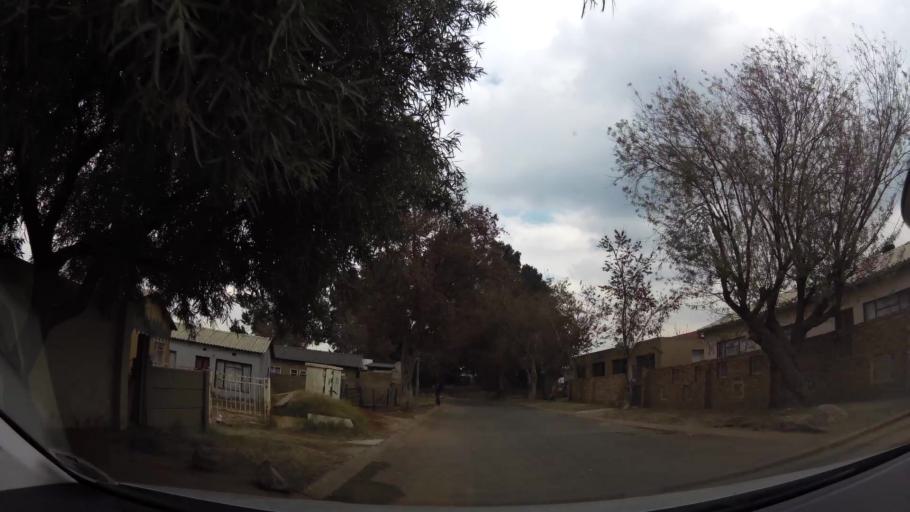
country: ZA
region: Gauteng
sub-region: City of Johannesburg Metropolitan Municipality
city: Soweto
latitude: -26.2655
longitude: 27.8624
